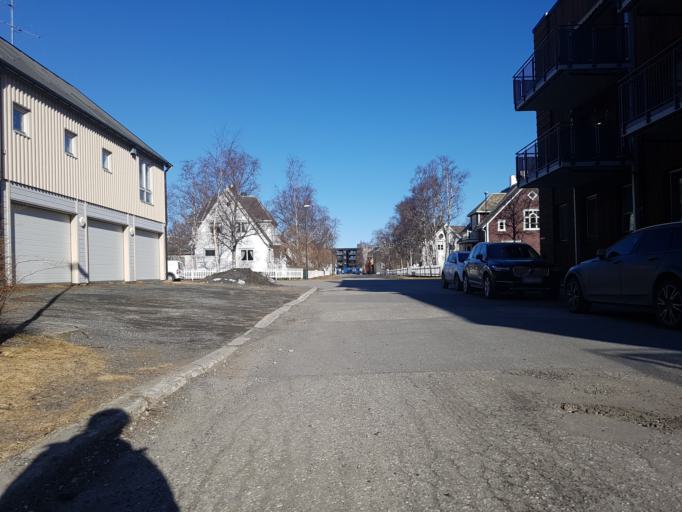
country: NO
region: Nordland
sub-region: Vefsn
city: Mosjoen
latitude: 65.8378
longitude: 13.1985
